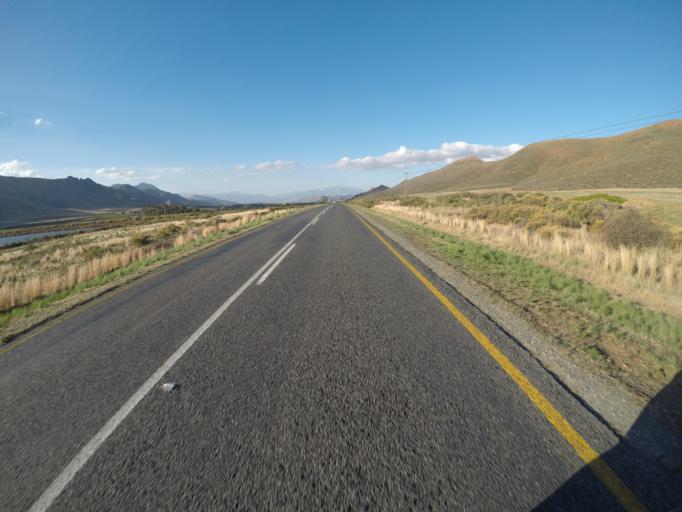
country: ZA
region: Western Cape
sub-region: Cape Winelands District Municipality
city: Worcester
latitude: -33.8608
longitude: 19.3738
